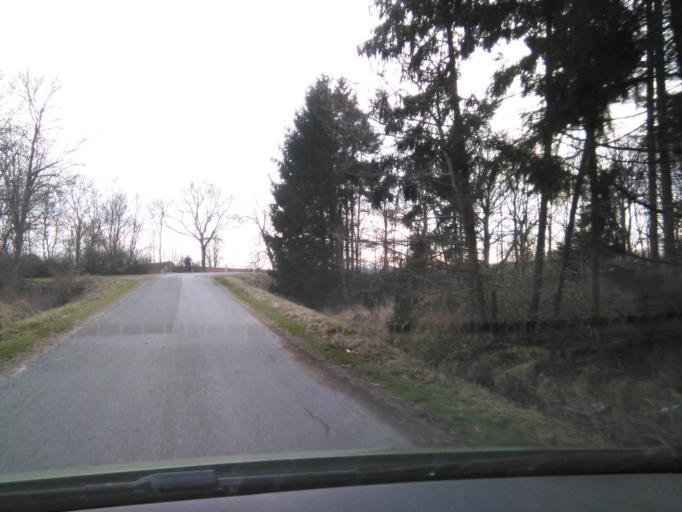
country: DK
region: Central Jutland
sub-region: Odder Kommune
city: Odder
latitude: 55.9246
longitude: 10.1077
